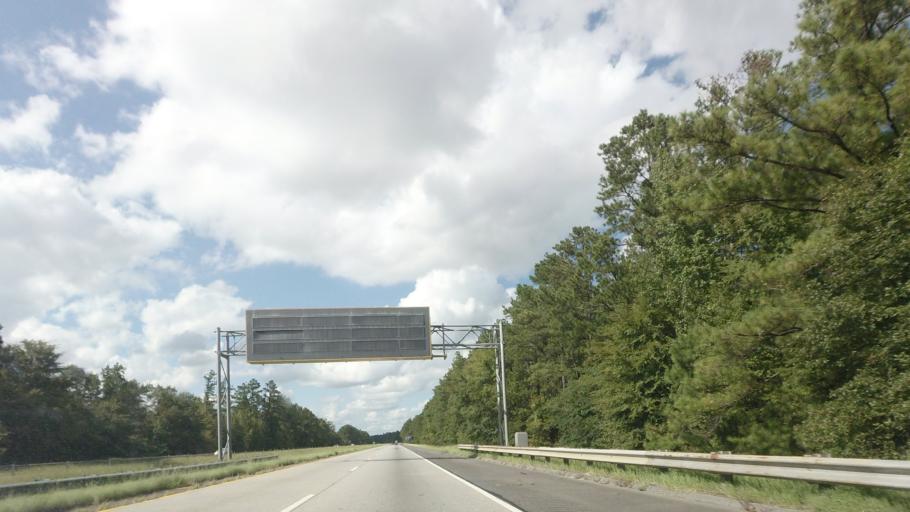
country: US
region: Georgia
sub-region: Bibb County
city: Macon
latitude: 32.7773
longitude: -83.5582
